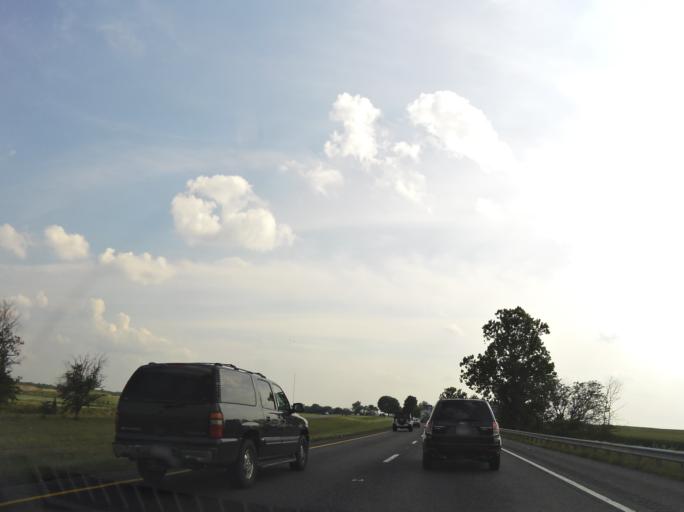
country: US
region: Pennsylvania
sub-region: Franklin County
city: State Line
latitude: 39.7146
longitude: -77.7403
